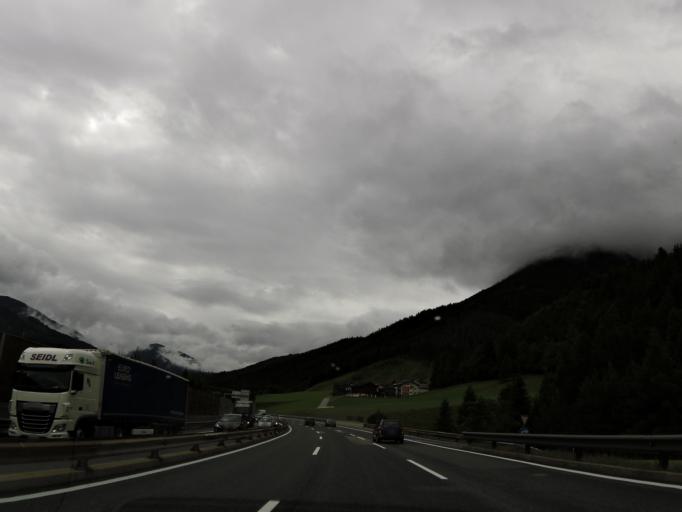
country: AT
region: Tyrol
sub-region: Politischer Bezirk Innsbruck Land
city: Matrei am Brenner
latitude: 47.1204
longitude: 11.4487
